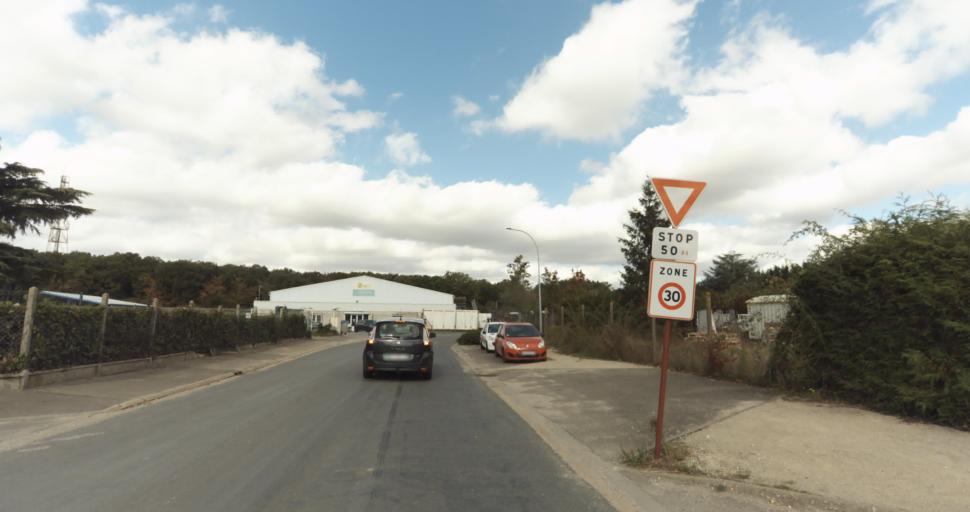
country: FR
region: Centre
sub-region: Departement d'Eure-et-Loir
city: Garnay
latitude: 48.7311
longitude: 1.3216
